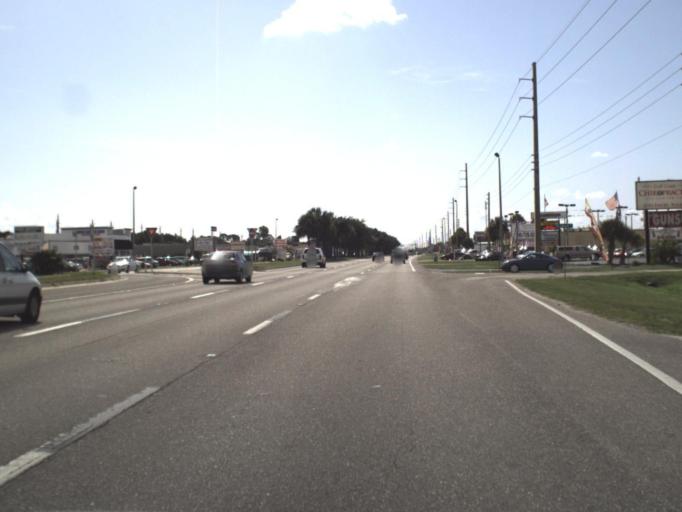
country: US
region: Florida
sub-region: Charlotte County
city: Port Charlotte
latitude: 26.9990
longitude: -82.1222
